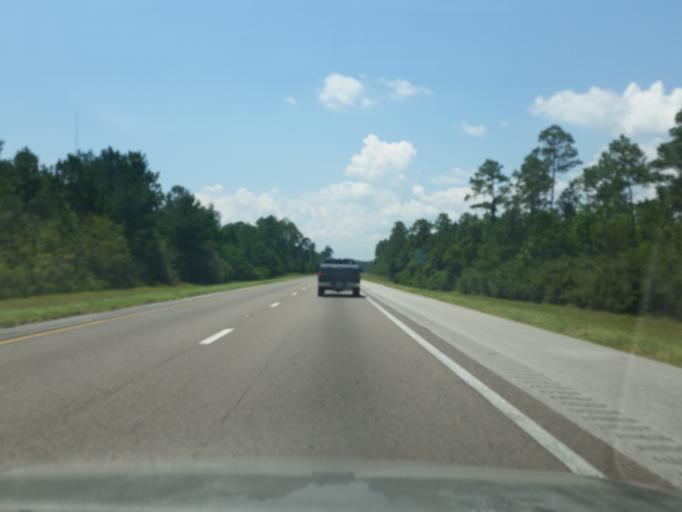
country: US
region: Alabama
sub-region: Baldwin County
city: Robertsdale
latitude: 30.5866
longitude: -87.5306
